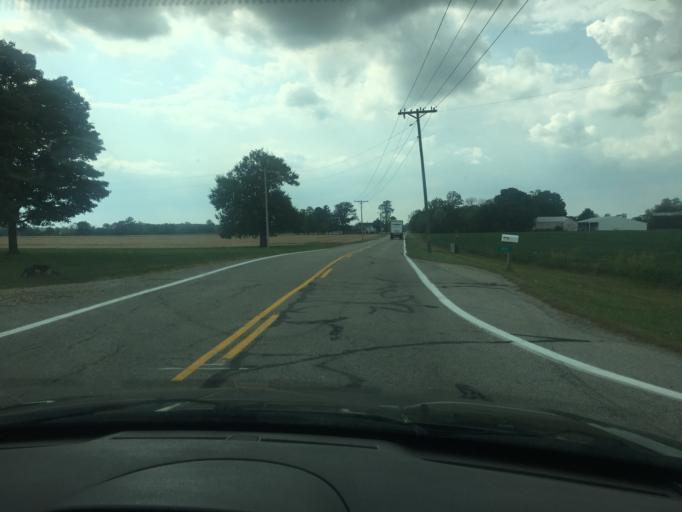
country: US
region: Ohio
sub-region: Champaign County
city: Urbana
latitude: 40.1584
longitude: -83.7993
